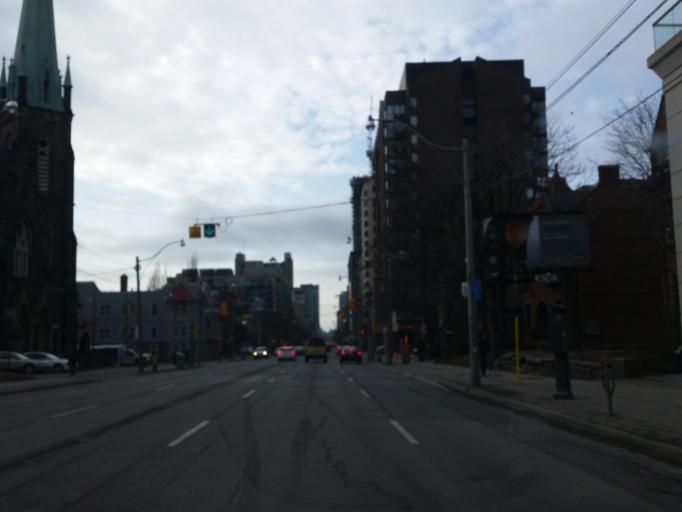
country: CA
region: Ontario
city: Toronto
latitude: 43.6611
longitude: -79.3762
